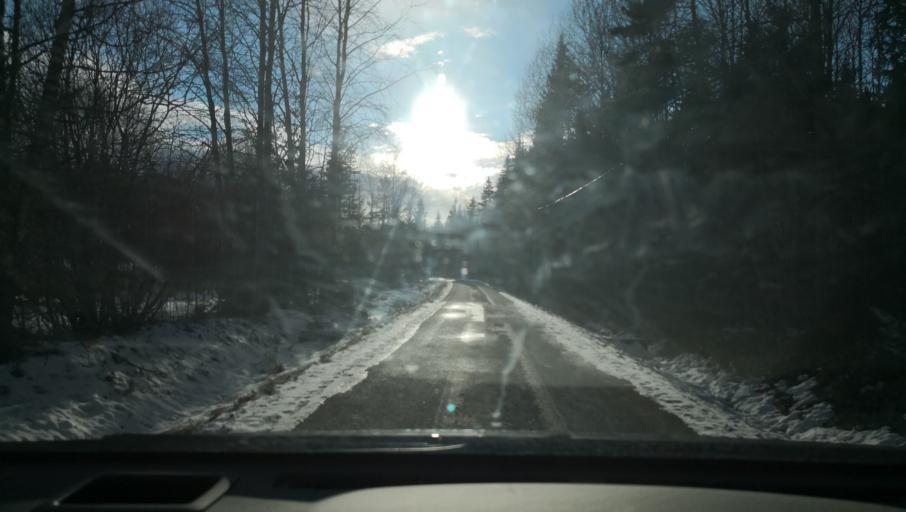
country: SE
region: Uppsala
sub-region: Enkopings Kommun
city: Irsta
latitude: 59.7042
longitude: 16.8736
